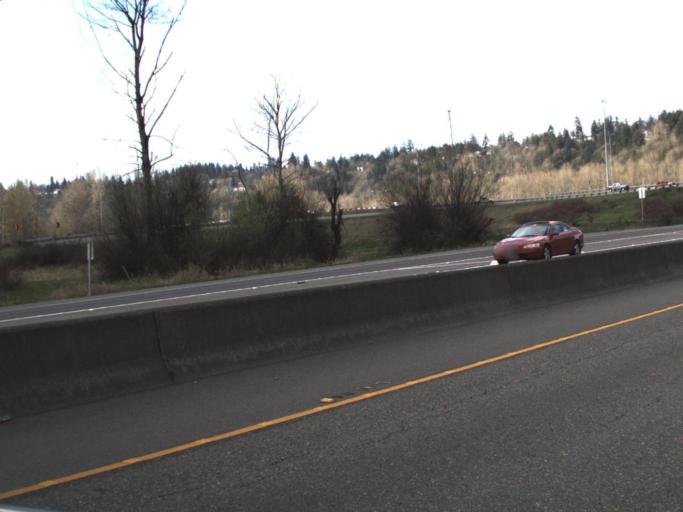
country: US
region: Washington
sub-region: King County
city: Auburn
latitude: 47.3025
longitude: -122.2489
